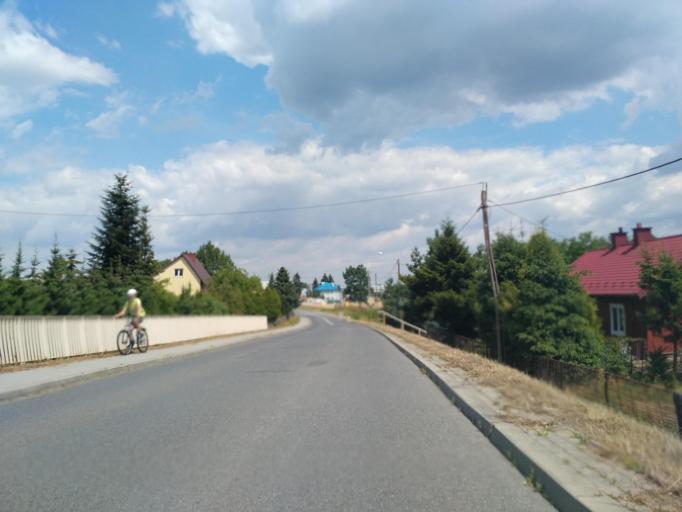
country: PL
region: Subcarpathian Voivodeship
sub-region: Powiat debicki
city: Pilzno
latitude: 49.9871
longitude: 21.2893
